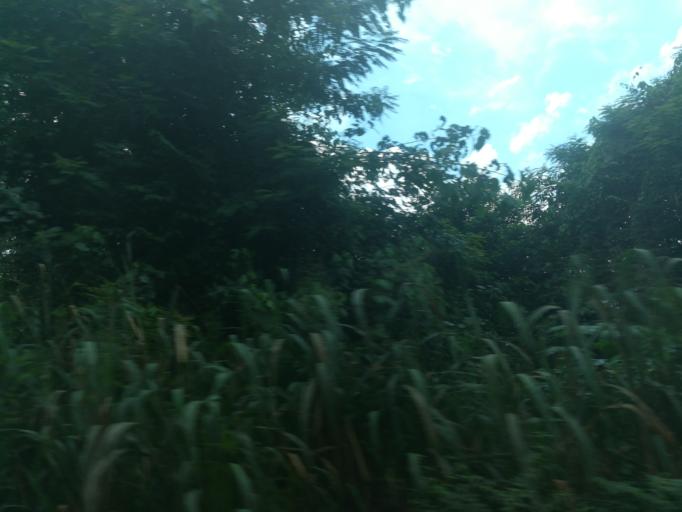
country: NG
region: Lagos
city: Ikorodu
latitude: 6.6637
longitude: 3.6345
